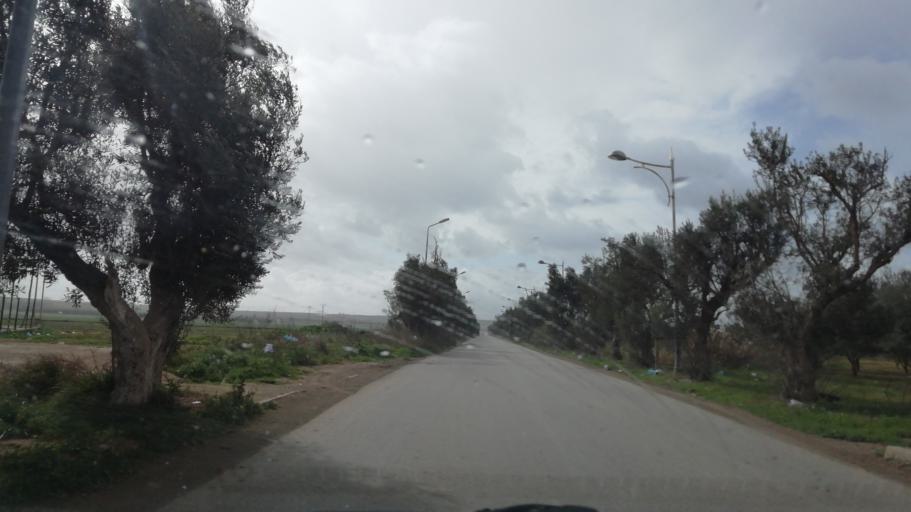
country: DZ
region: Oran
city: Sidi ech Chahmi
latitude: 35.6542
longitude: -0.5221
